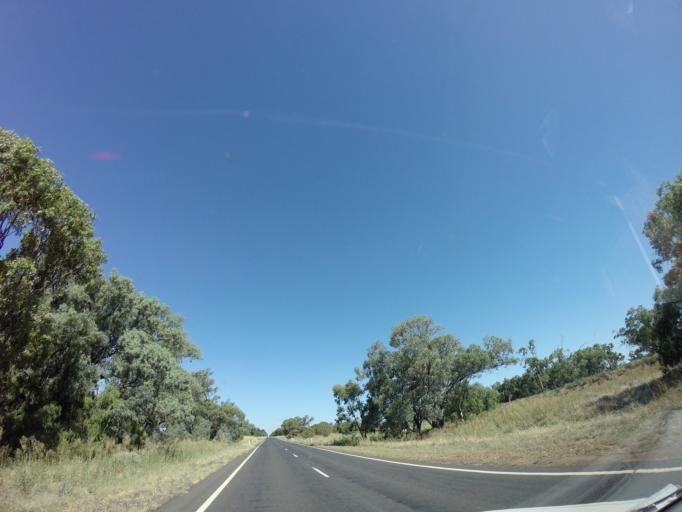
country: AU
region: New South Wales
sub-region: Bogan
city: Nyngan
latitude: -31.7979
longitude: 147.6418
